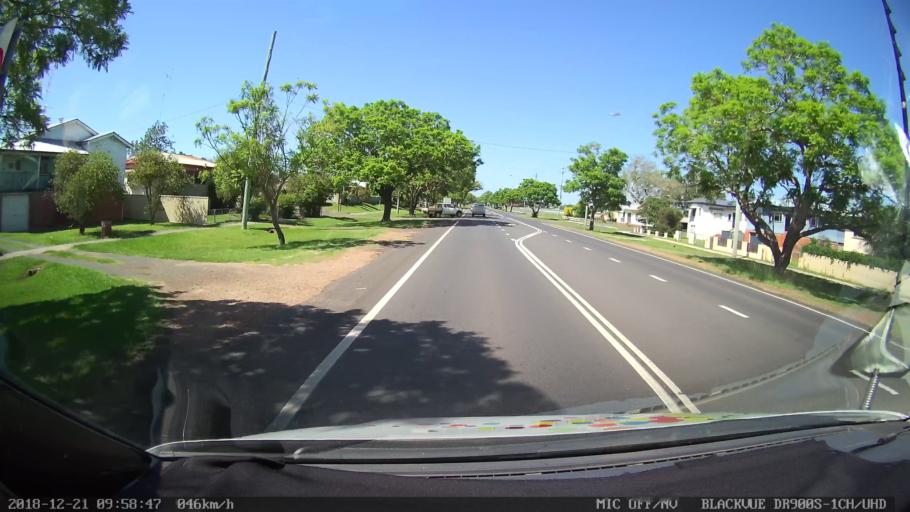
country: AU
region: New South Wales
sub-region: Clarence Valley
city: Grafton
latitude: -29.6745
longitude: 152.9338
